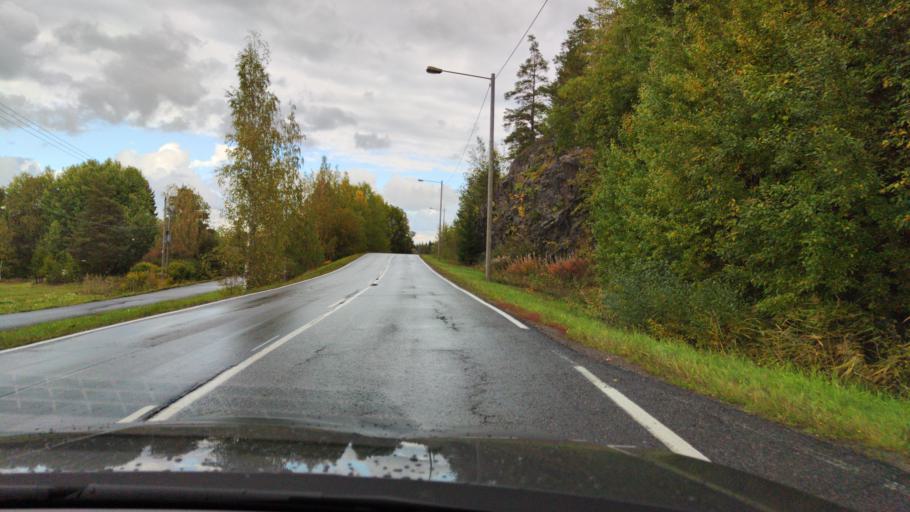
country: FI
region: Varsinais-Suomi
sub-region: Turku
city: Turku
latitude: 60.3651
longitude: 22.2022
